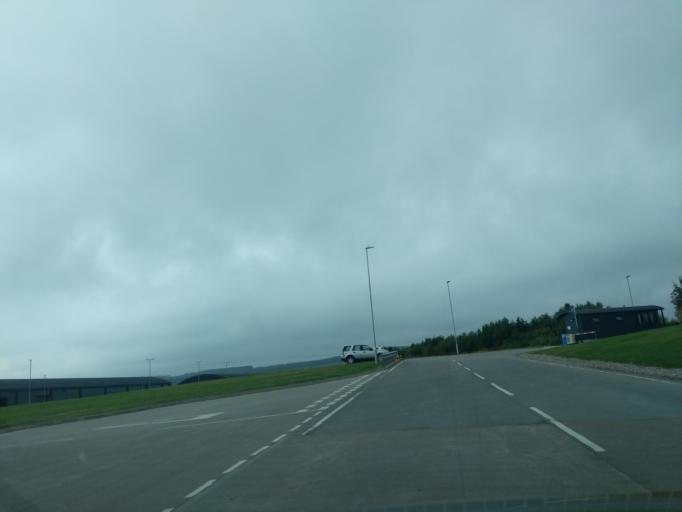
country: GB
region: Scotland
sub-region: Moray
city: Rothes
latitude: 57.4906
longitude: -3.2129
